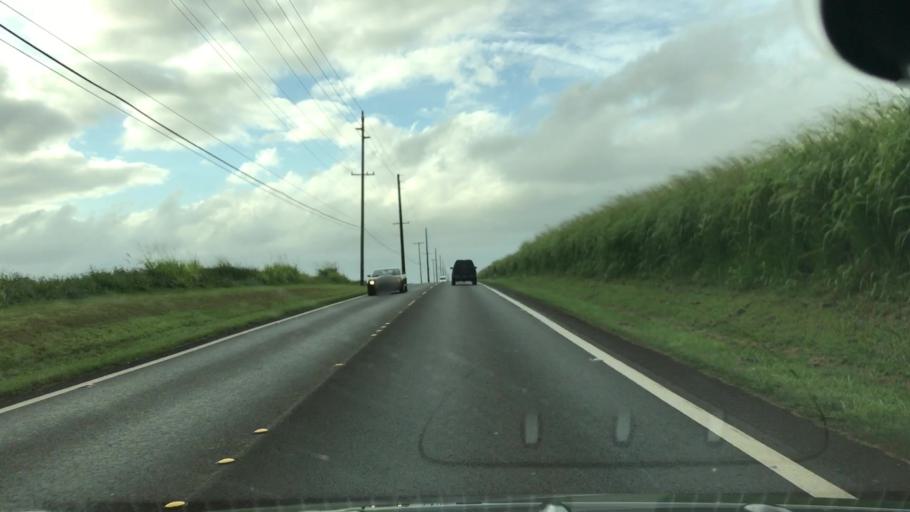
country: US
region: Hawaii
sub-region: Honolulu County
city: Whitmore Village
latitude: 21.5298
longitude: -158.0401
